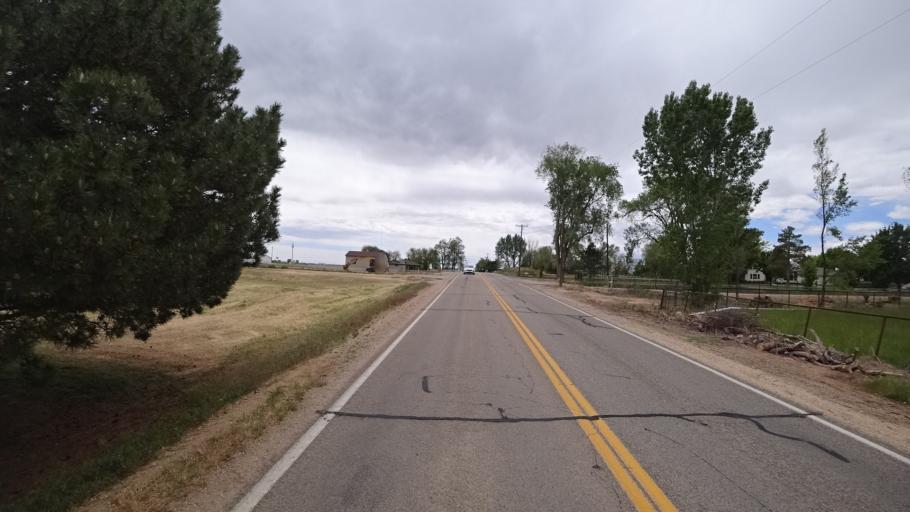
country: US
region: Idaho
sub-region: Ada County
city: Meridian
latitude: 43.5557
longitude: -116.4139
